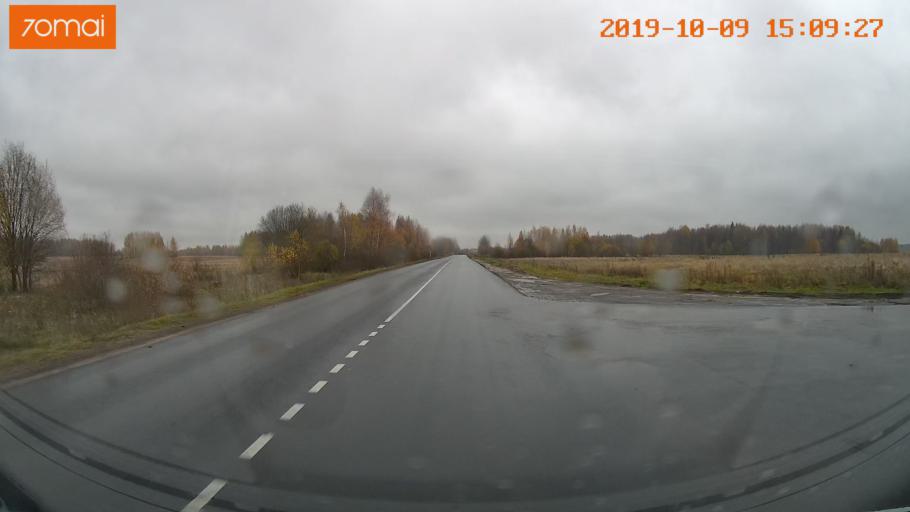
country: RU
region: Kostroma
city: Susanino
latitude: 58.1913
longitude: 41.6502
